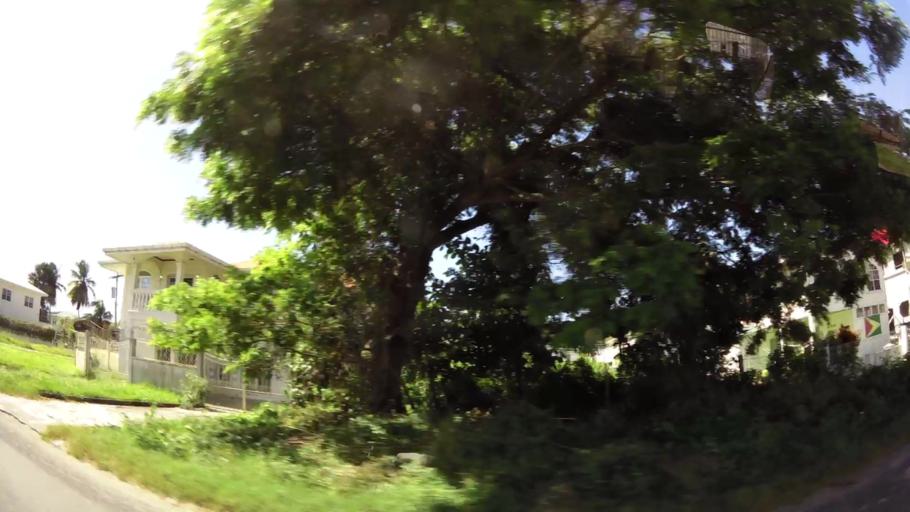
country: GY
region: Demerara-Mahaica
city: Georgetown
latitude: 6.8079
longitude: -58.1323
